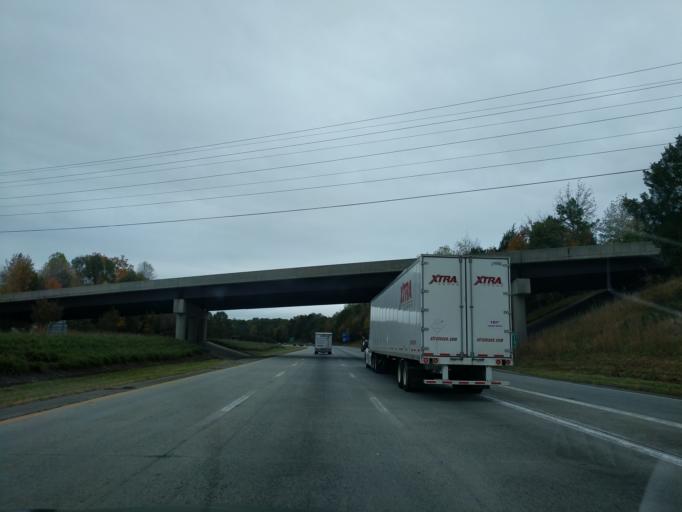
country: US
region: North Carolina
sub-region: Davidson County
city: Thomasville
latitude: 35.8544
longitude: -80.0984
